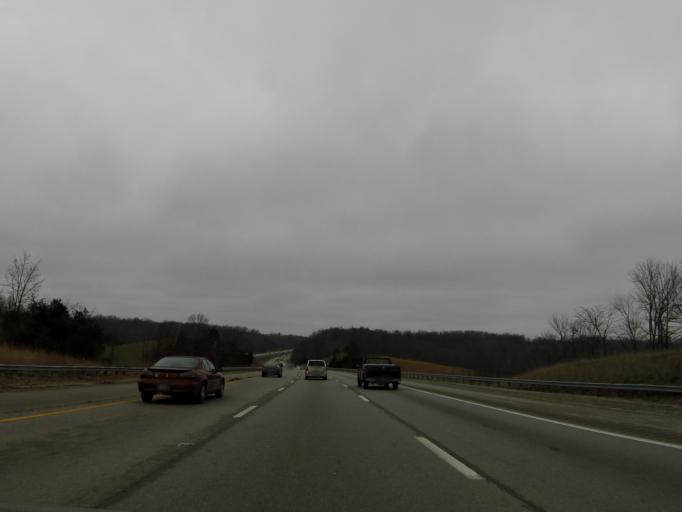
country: US
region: Kentucky
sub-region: Grant County
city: Williamstown
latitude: 38.4542
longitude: -84.5752
